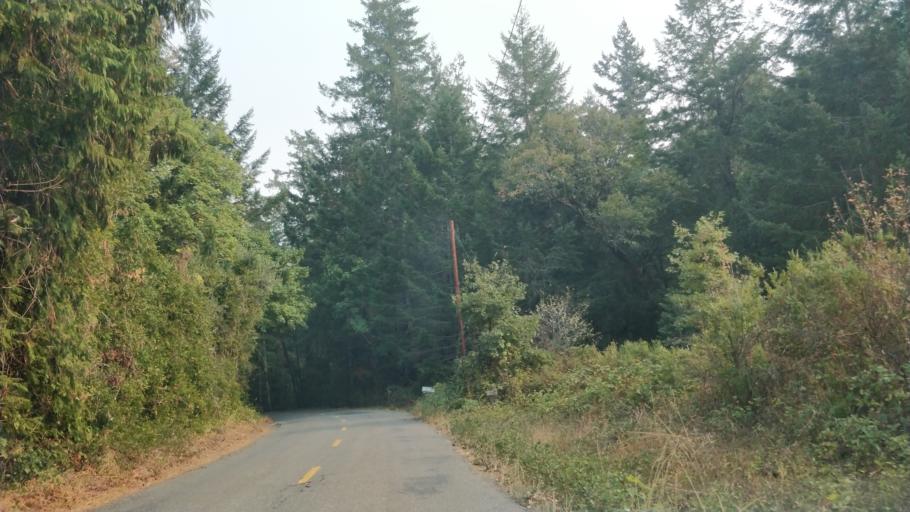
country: US
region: California
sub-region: Humboldt County
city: Rio Dell
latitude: 40.2360
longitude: -124.1586
